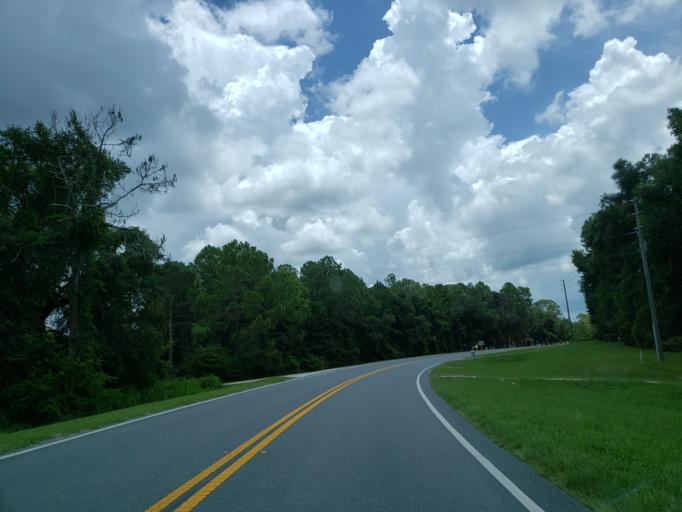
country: US
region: Florida
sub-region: Hernando County
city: Ridge Manor
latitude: 28.6103
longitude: -82.2078
